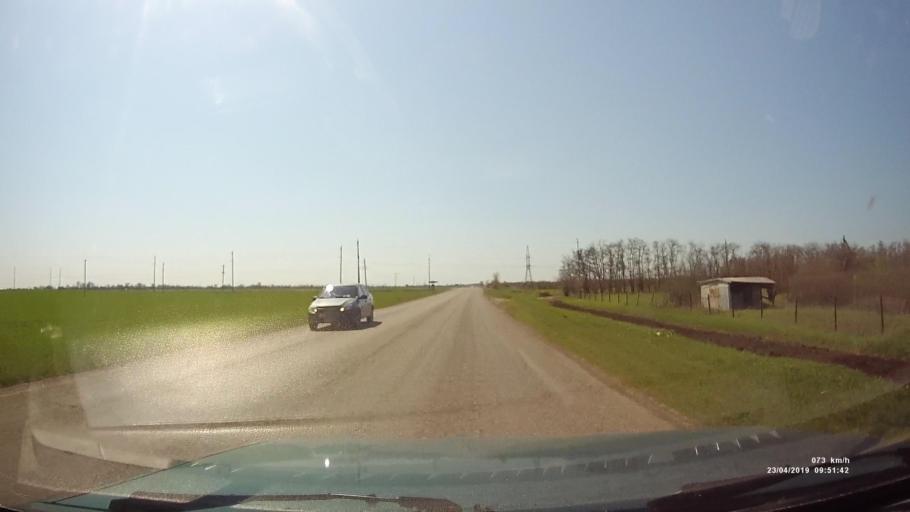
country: RU
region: Rostov
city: Orlovskiy
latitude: 46.8529
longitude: 42.0422
